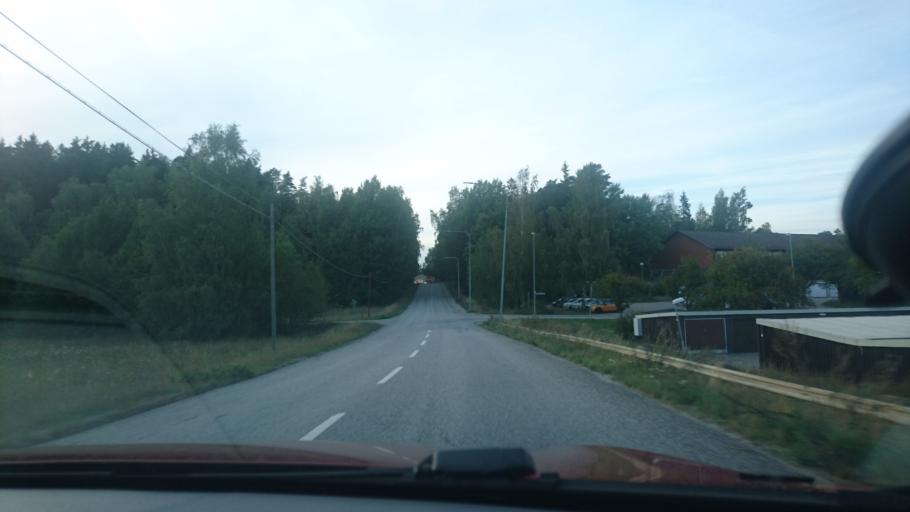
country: SE
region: Stockholm
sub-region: Sodertalje Kommun
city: Pershagen
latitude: 59.1509
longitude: 17.6512
